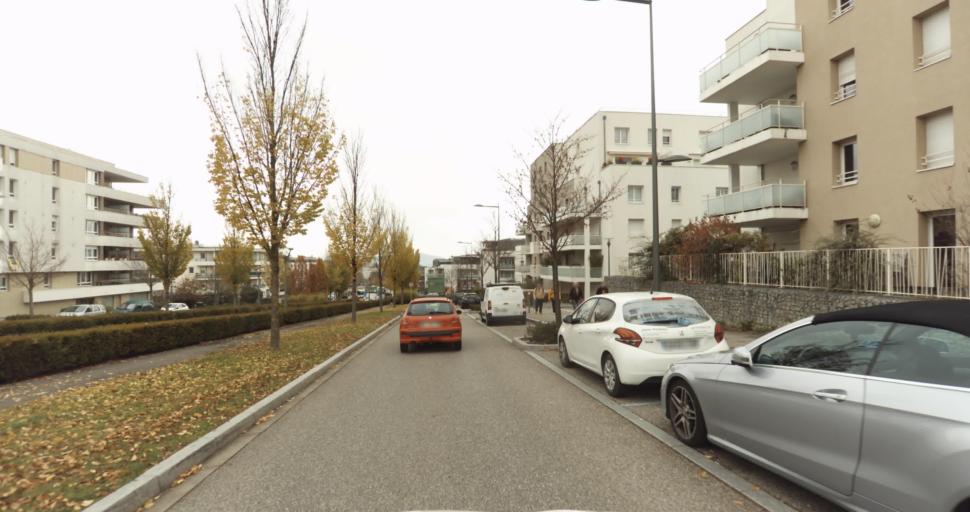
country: FR
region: Rhone-Alpes
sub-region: Departement de la Haute-Savoie
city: Seynod
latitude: 45.8806
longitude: 6.0991
